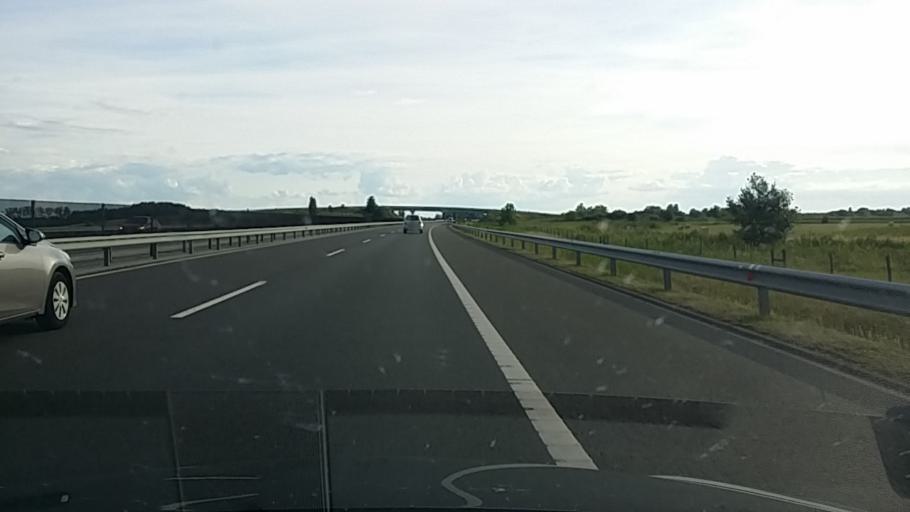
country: HU
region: Hajdu-Bihar
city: Gorbehaza
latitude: 47.8008
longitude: 21.2901
